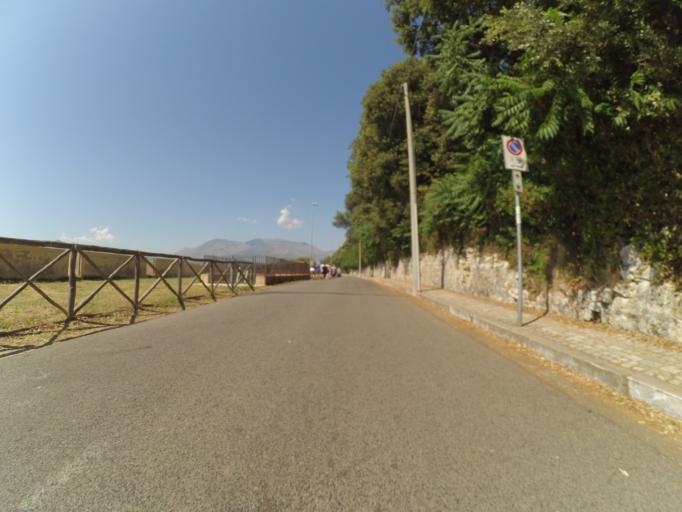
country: IT
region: Latium
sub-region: Provincia di Latina
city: Gaeta
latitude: 41.2080
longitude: 13.5724
